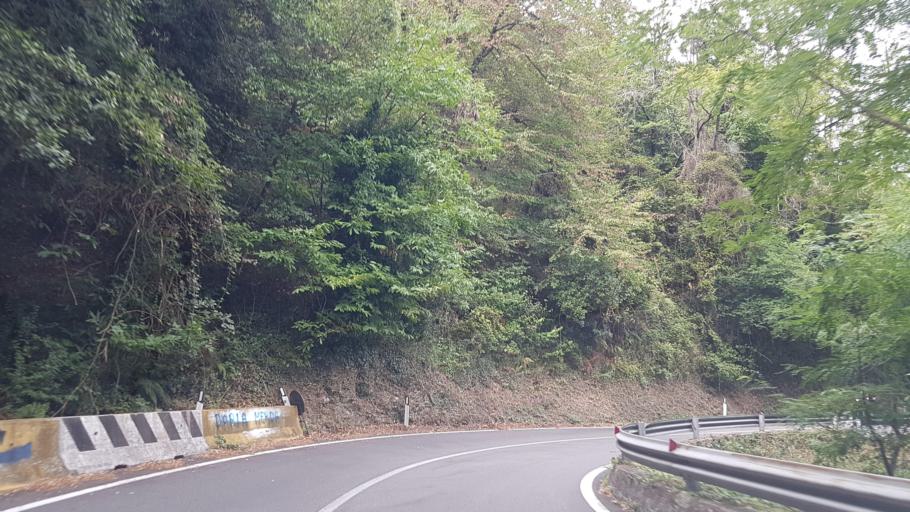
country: IT
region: Liguria
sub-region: Provincia di Genova
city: Casarza Ligure
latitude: 44.2561
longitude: 9.4627
